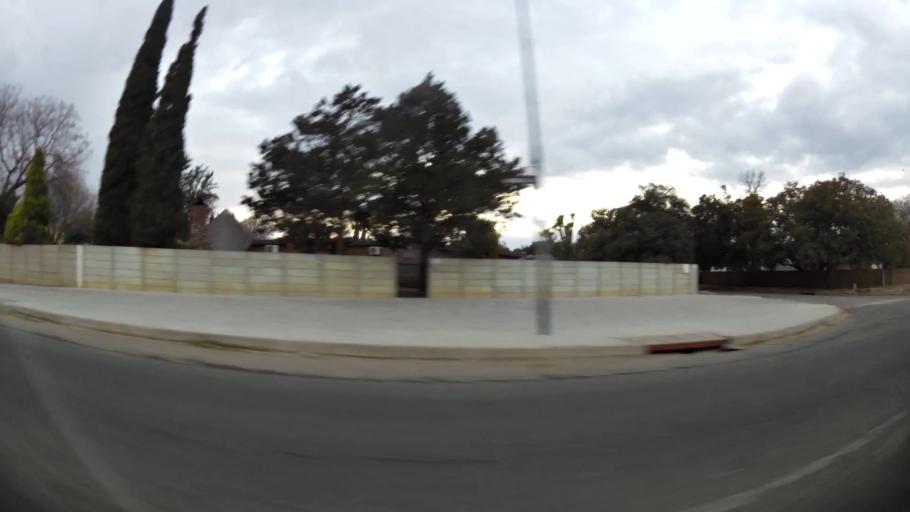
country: ZA
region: Orange Free State
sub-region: Lejweleputswa District Municipality
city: Welkom
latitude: -27.9707
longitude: 26.7249
